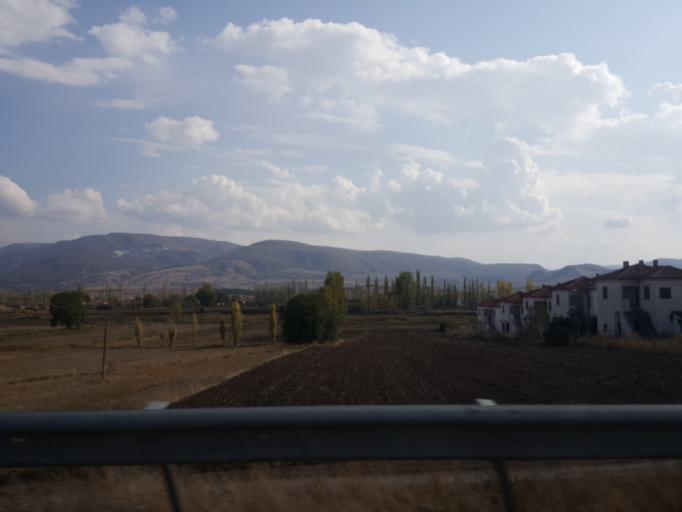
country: TR
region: Corum
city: Seydim
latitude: 40.4340
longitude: 34.8004
